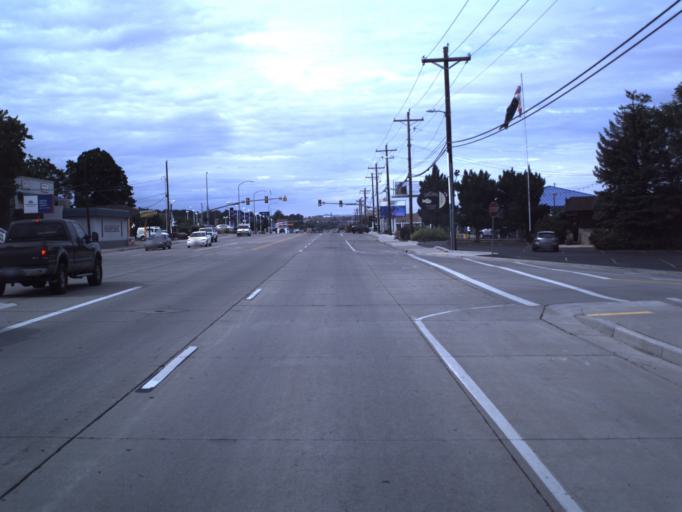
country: US
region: Utah
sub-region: Weber County
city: South Ogden
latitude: 41.1955
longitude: -111.9763
